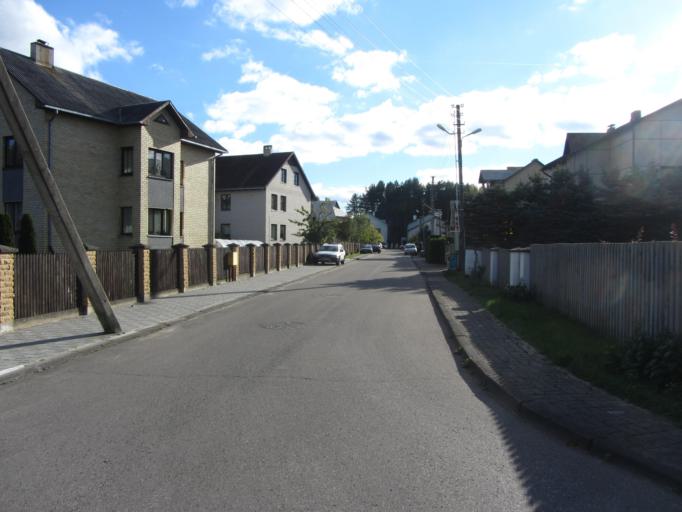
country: LT
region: Vilnius County
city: Lazdynai
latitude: 54.6665
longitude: 25.2196
